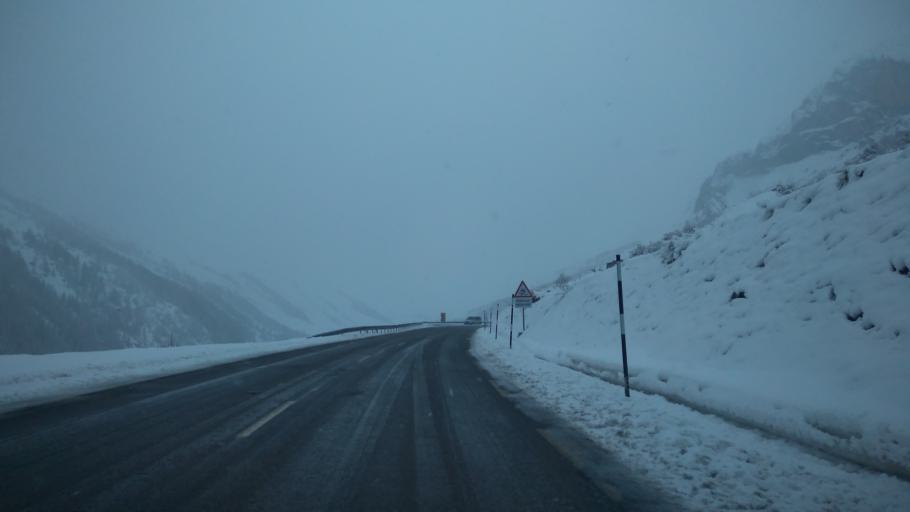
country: FR
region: Provence-Alpes-Cote d'Azur
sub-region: Departement des Hautes-Alpes
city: Le Monetier-les-Bains
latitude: 45.0149
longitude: 6.4665
